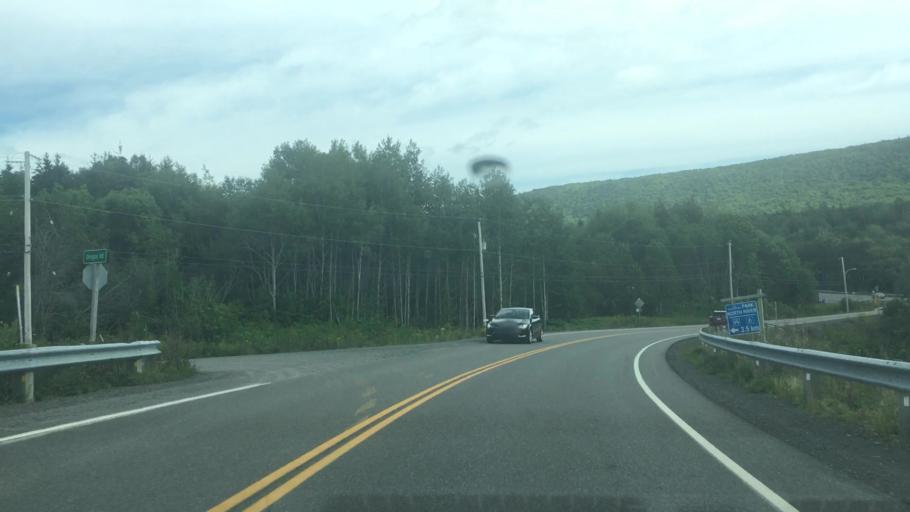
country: CA
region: Nova Scotia
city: Sydney Mines
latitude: 46.3082
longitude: -60.6217
